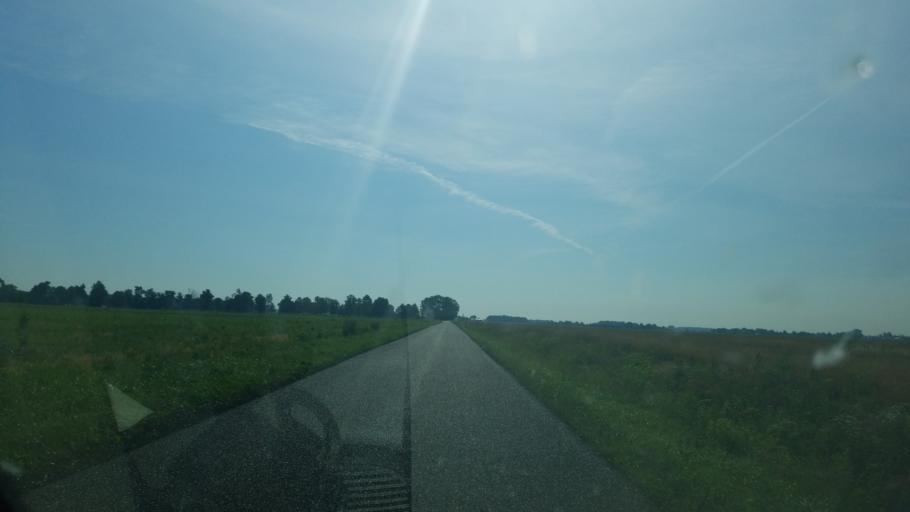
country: US
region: Ohio
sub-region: Hancock County
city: Findlay
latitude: 41.0214
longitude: -83.5408
